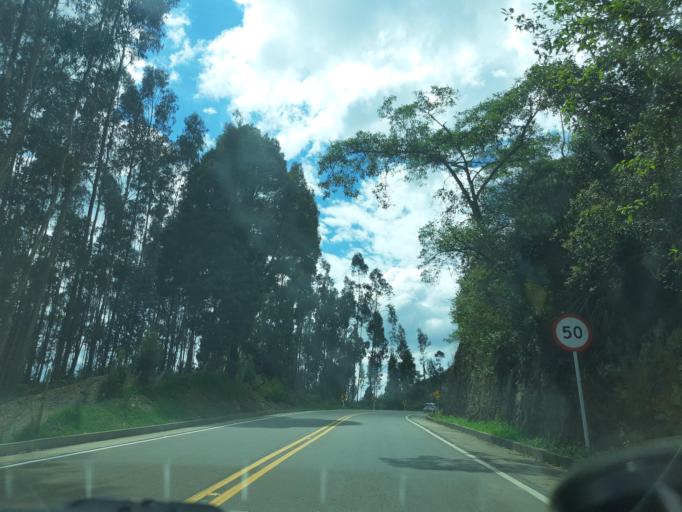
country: CO
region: Boyaca
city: Raquira
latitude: 5.5897
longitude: -73.6963
